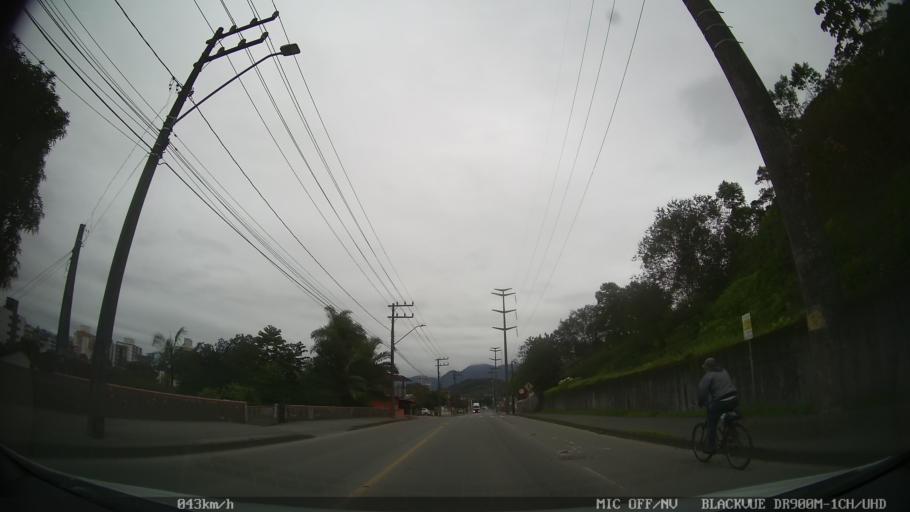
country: BR
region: Santa Catarina
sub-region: Joinville
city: Joinville
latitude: -26.2661
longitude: -48.8793
